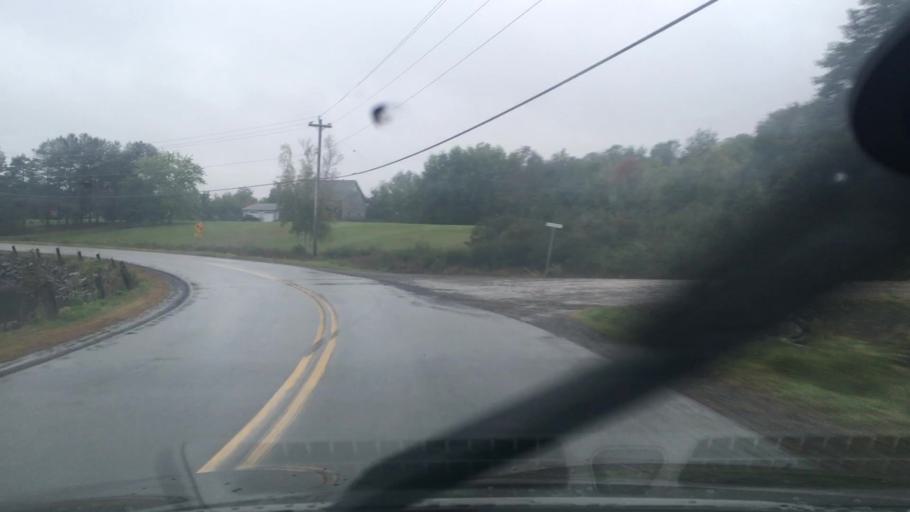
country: CA
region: Nova Scotia
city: Windsor
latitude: 44.8404
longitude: -64.2378
